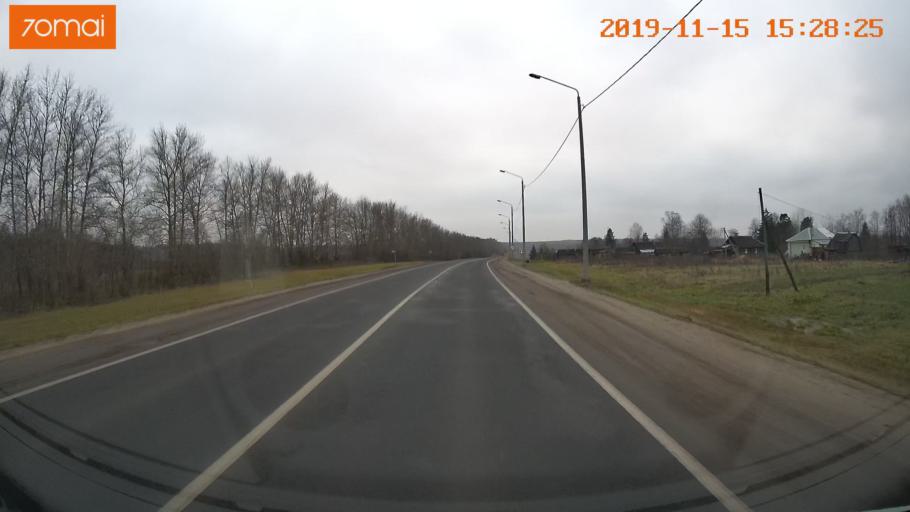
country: RU
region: Jaroslavl
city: Danilov
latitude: 58.1323
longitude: 40.1351
